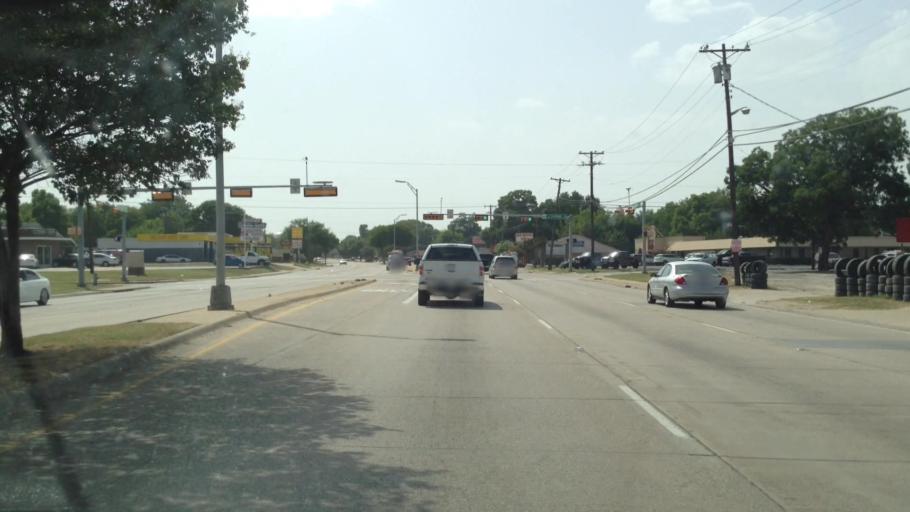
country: US
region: Texas
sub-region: Collin County
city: McKinney
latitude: 33.2150
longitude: -96.6194
